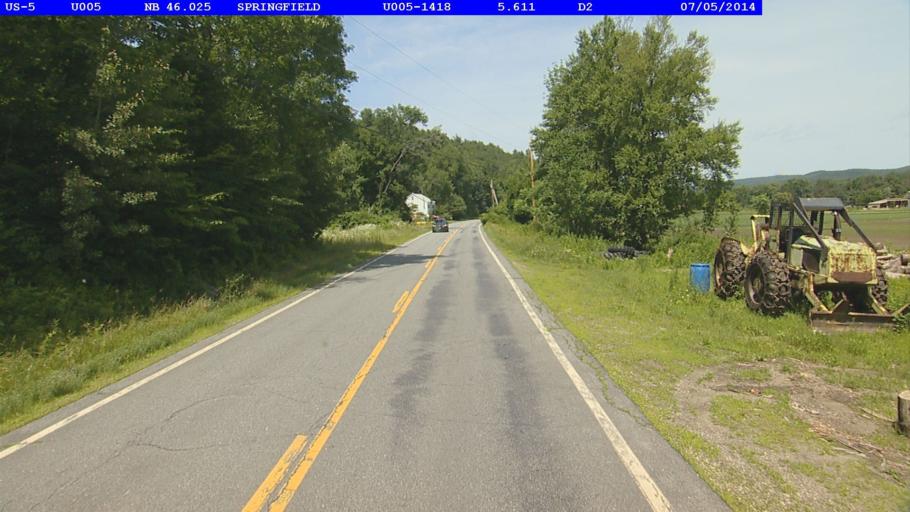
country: US
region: New Hampshire
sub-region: Sullivan County
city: Charlestown
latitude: 43.2942
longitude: -72.4107
